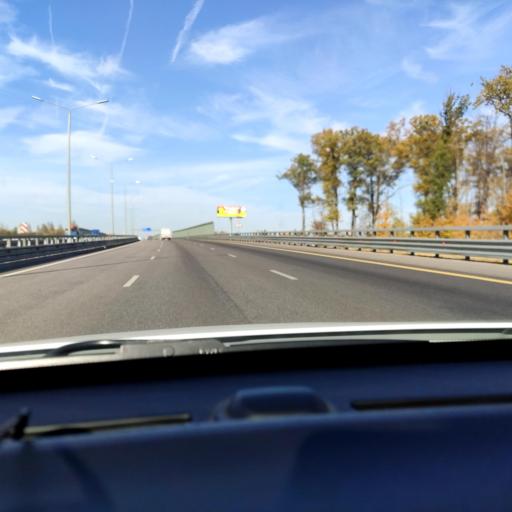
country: RU
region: Voronezj
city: Podgornoye
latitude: 51.8145
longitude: 39.2523
